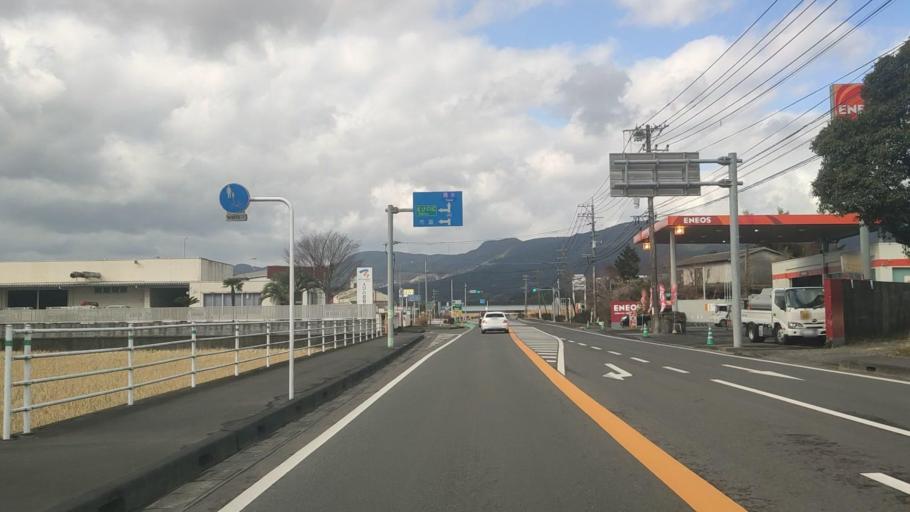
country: JP
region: Kumamoto
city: Hitoyoshi
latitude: 32.0512
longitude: 130.8056
